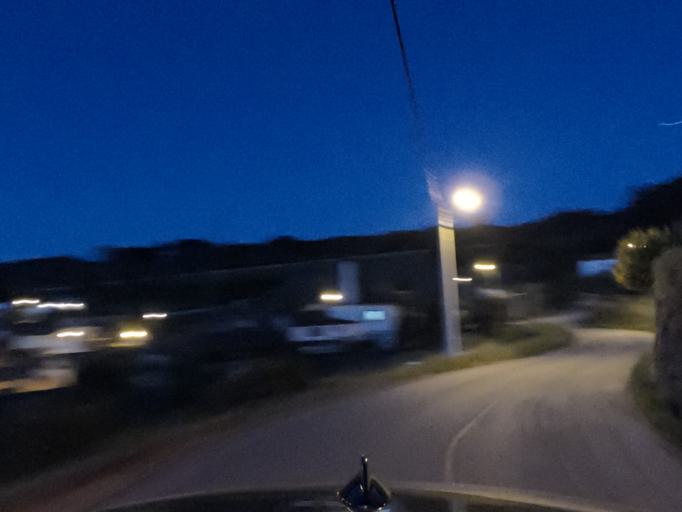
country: PT
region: Vila Real
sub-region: Vila Real
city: Vila Real
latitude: 41.3305
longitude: -7.7021
